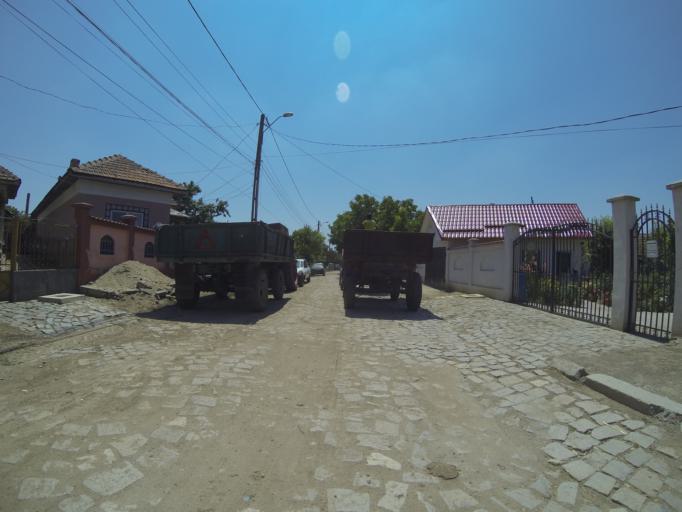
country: RO
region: Dolj
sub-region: Comuna Segarcea
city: Segarcea
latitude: 44.0901
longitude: 23.7534
